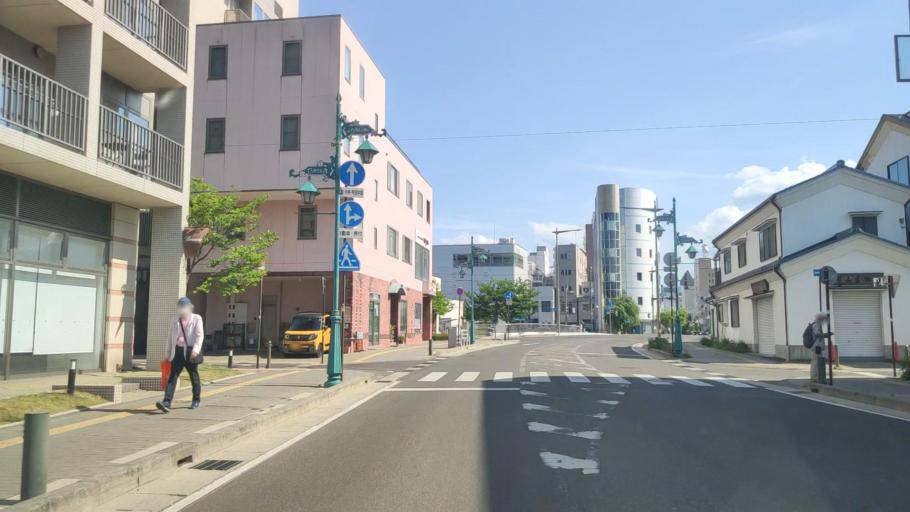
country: JP
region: Nagano
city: Matsumoto
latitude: 36.2346
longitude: 137.9676
